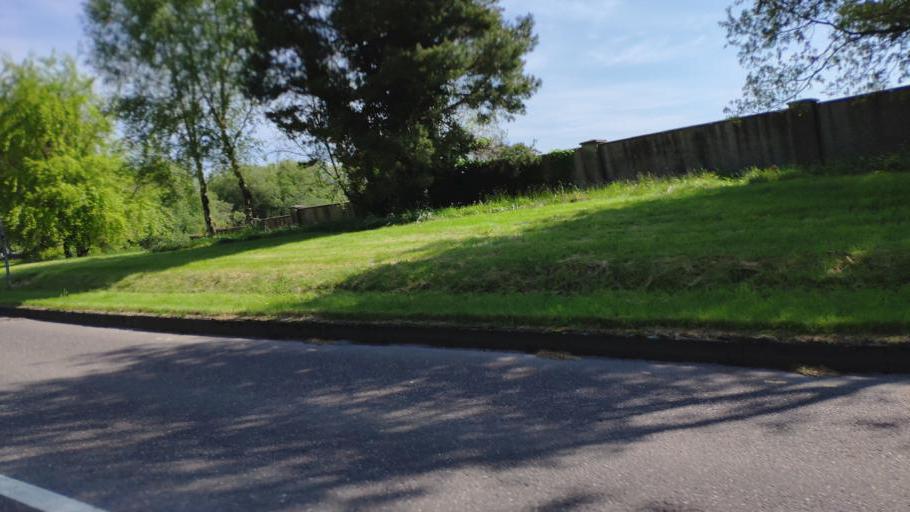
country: IE
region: Munster
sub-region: County Cork
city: Blarney
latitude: 51.9275
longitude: -8.5574
